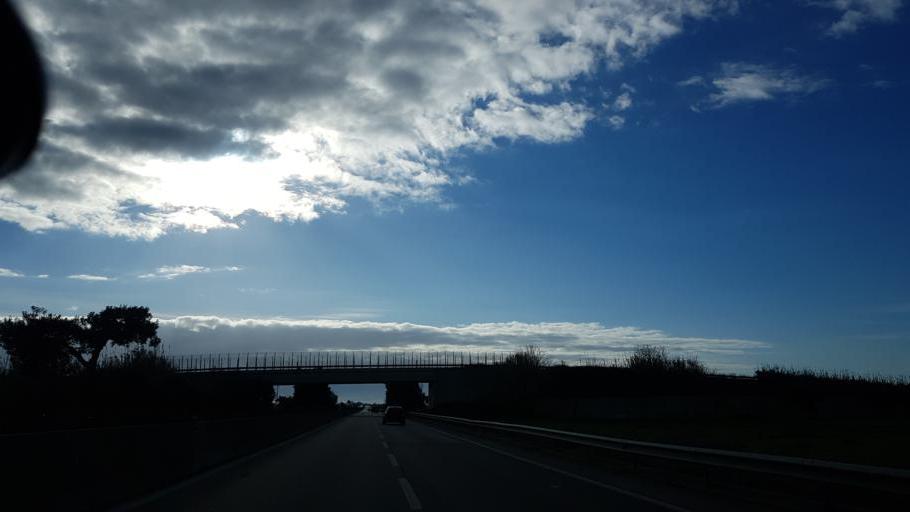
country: IT
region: Apulia
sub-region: Provincia di Brindisi
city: La Rosa
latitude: 40.5773
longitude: 17.9800
